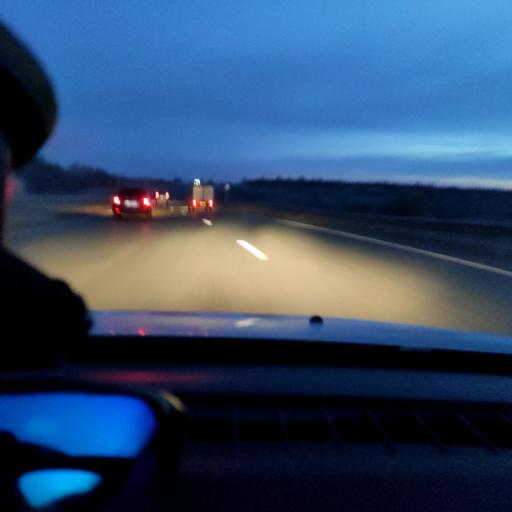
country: RU
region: Samara
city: Novokuybyshevsk
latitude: 53.0580
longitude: 50.0191
